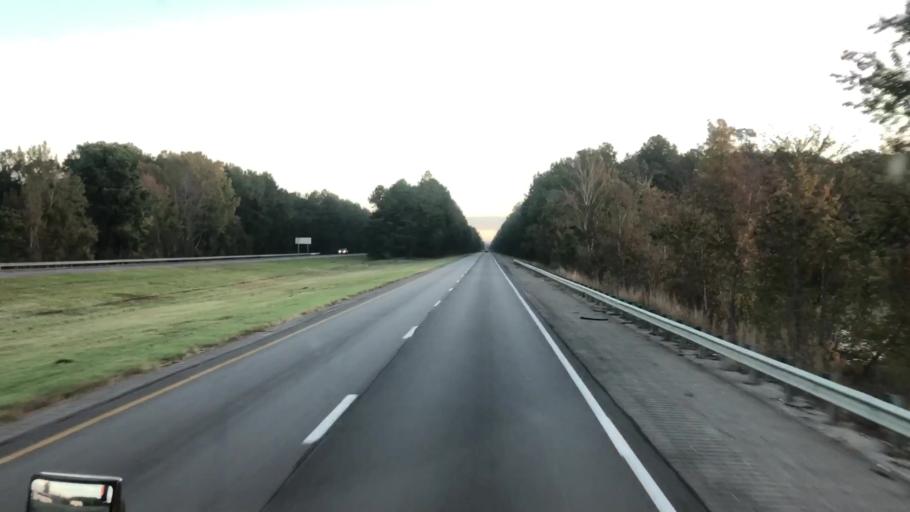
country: US
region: South Carolina
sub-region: Orangeburg County
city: Holly Hill
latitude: 33.5324
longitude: -80.4216
